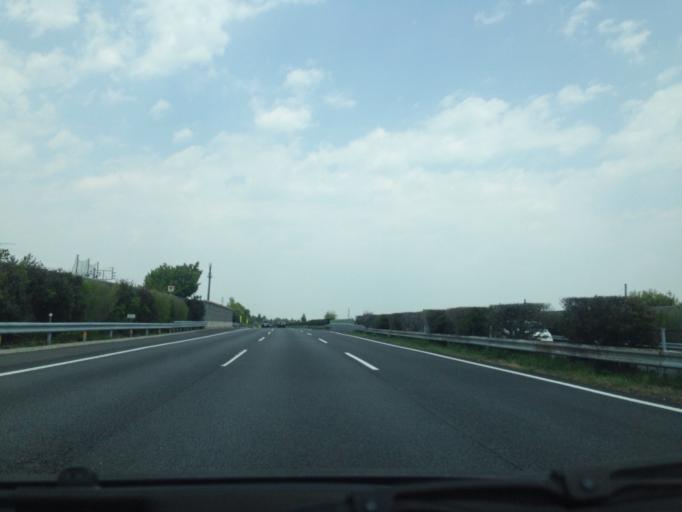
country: JP
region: Tochigi
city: Utsunomiya-shi
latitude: 36.5831
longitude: 139.8349
